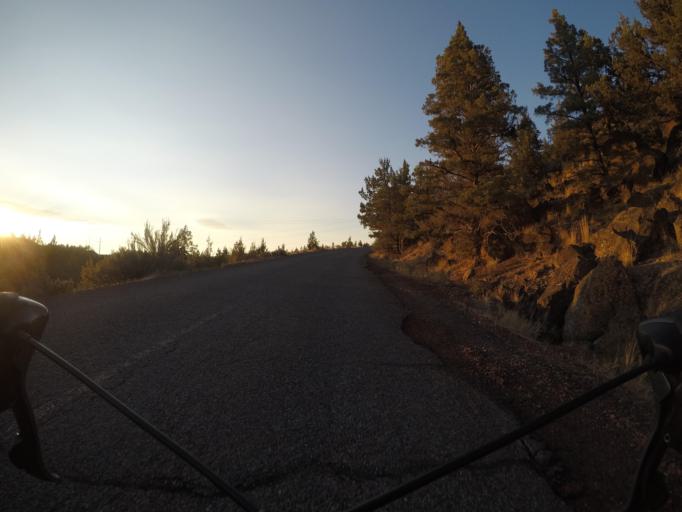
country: US
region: Oregon
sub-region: Deschutes County
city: Redmond
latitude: 44.2718
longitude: -121.2567
